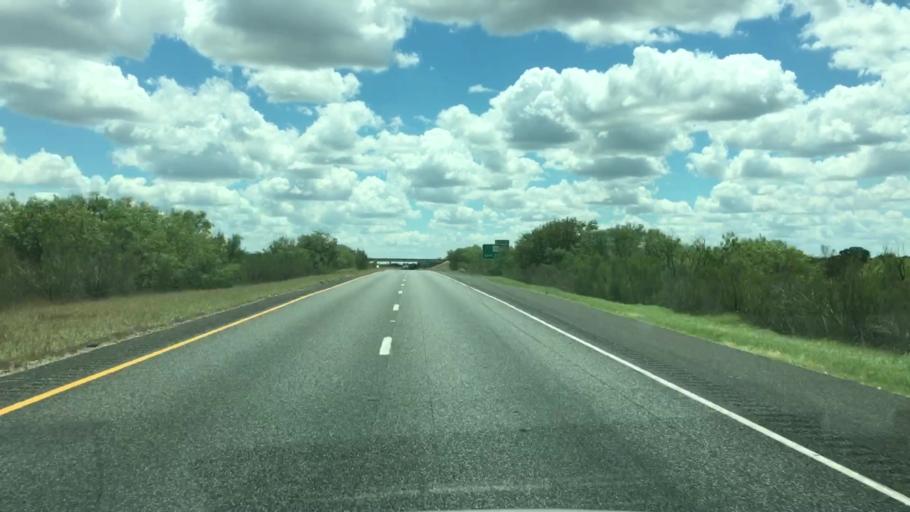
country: US
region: Texas
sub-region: Atascosa County
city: Pleasanton
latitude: 28.9226
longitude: -98.4353
